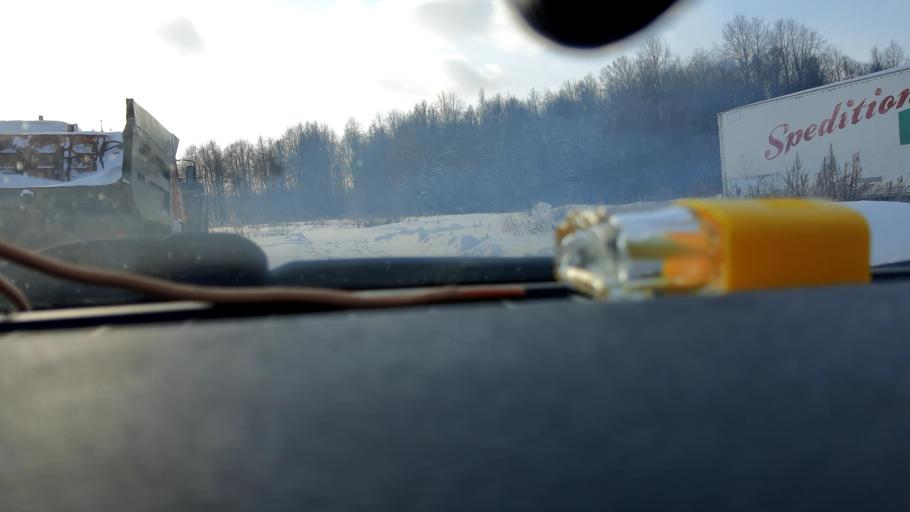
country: RU
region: Bashkortostan
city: Kabakovo
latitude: 54.6339
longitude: 56.0629
